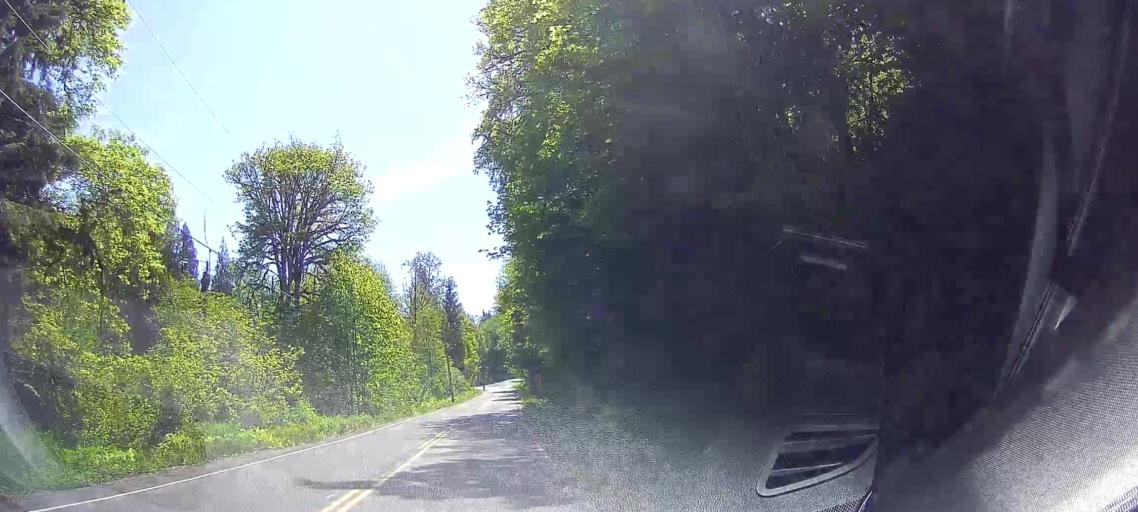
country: US
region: Washington
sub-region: Snohomish County
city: Darrington
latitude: 48.4743
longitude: -121.6443
